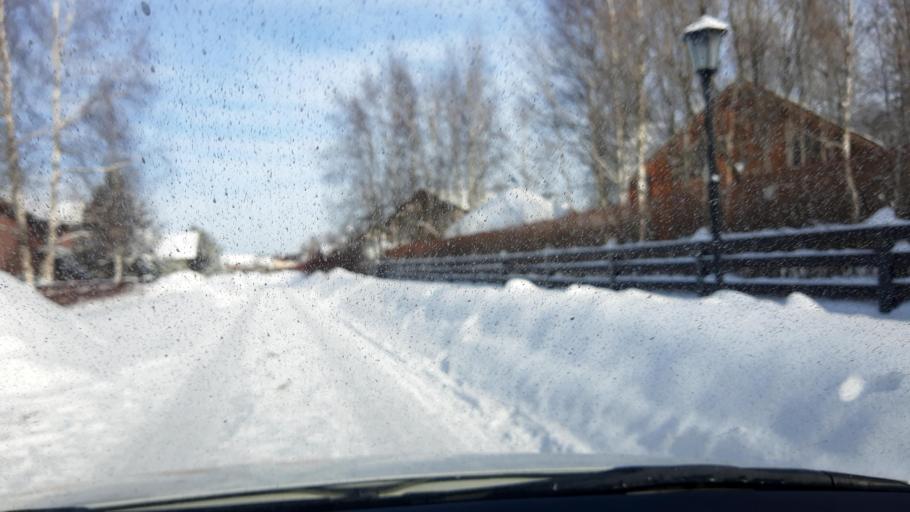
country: RU
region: Moskovskaya
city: Rumyantsevo
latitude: 55.9146
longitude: 36.5810
